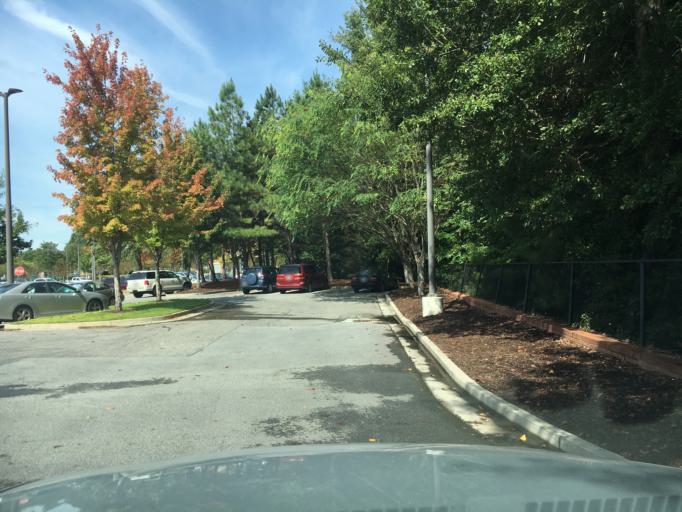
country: US
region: Georgia
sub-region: Fulton County
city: Johns Creek
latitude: 34.0136
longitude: -84.1829
